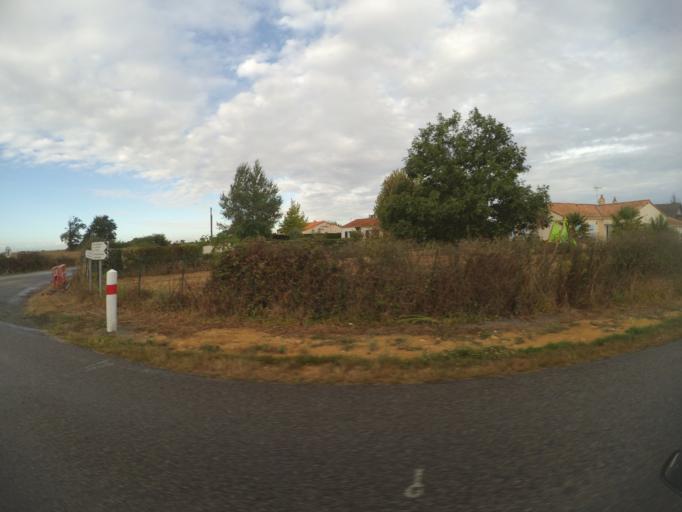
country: FR
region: Pays de la Loire
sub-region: Departement de la Loire-Atlantique
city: La Planche
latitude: 47.0364
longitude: -1.4173
